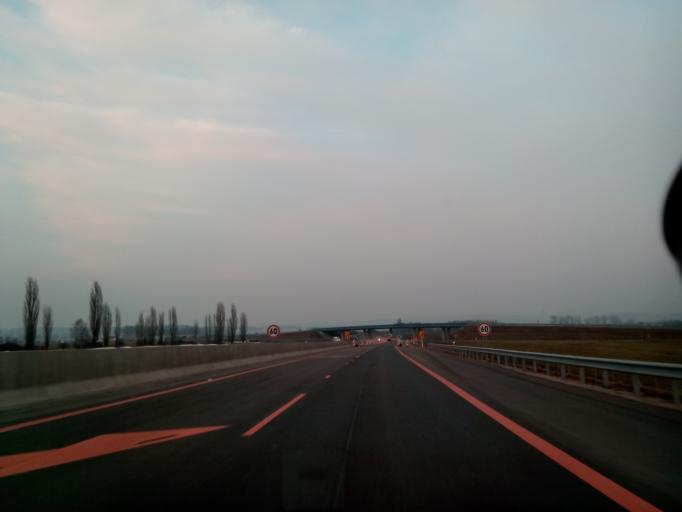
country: SK
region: Kosicky
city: Kosice
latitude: 48.6412
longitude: 21.2650
